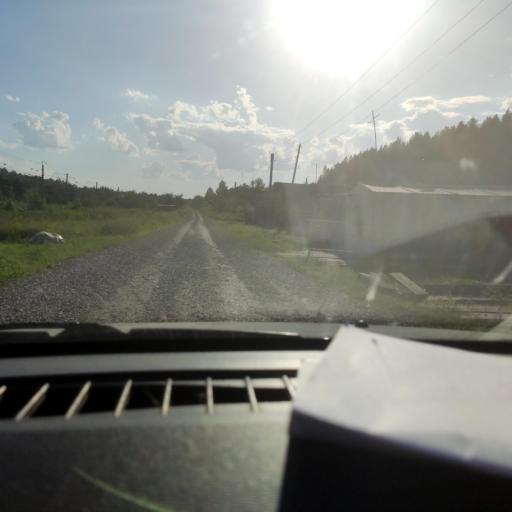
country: RU
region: Perm
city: Krasnokamsk
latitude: 58.1357
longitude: 55.6637
